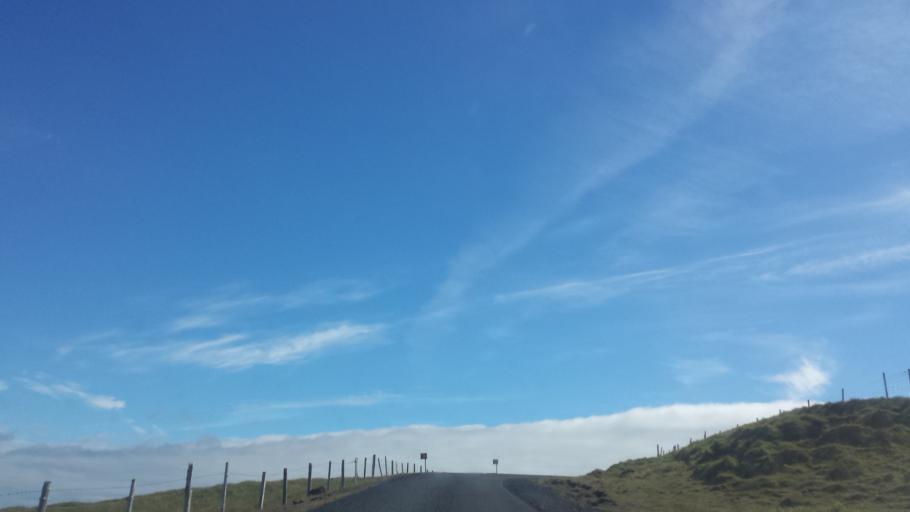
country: IS
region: South
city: Vestmannaeyjar
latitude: 63.4024
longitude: -20.2826
